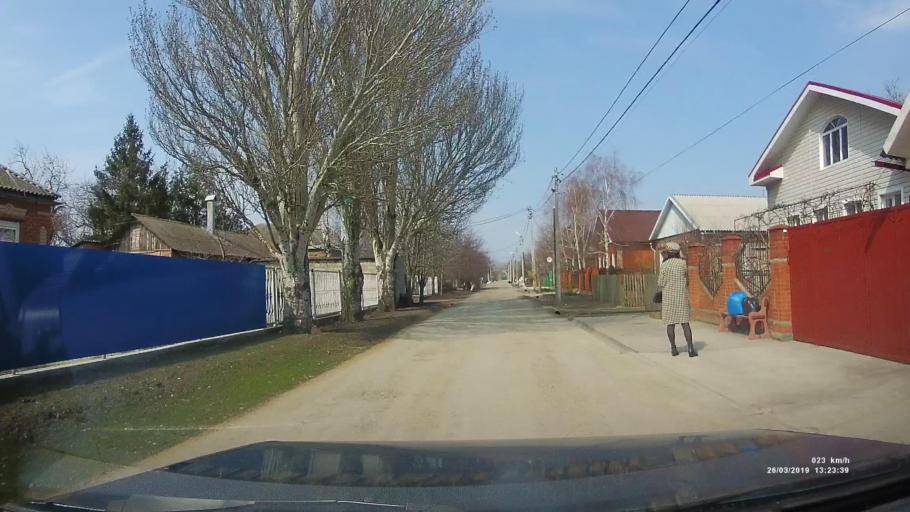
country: RU
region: Rostov
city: Novobessergenovka
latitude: 47.1726
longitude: 38.7667
